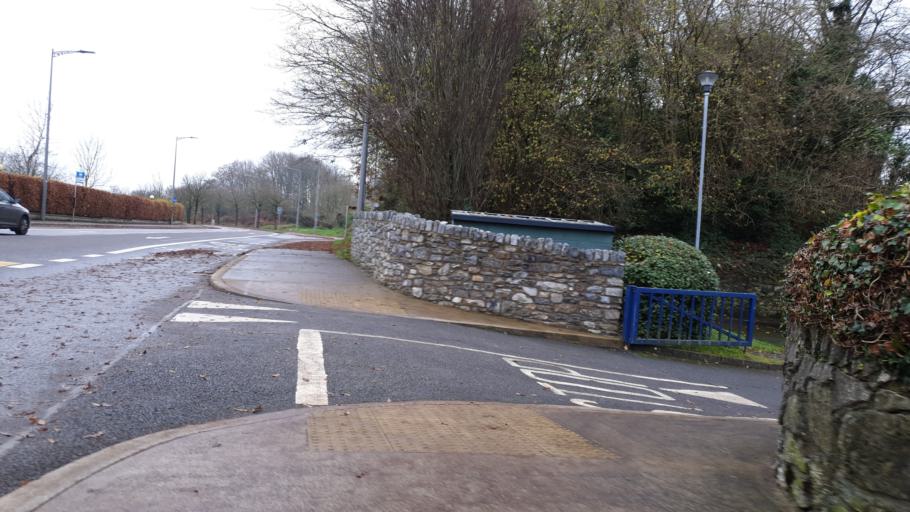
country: IE
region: Munster
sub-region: County Cork
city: Cork
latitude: 51.8900
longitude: -8.4104
